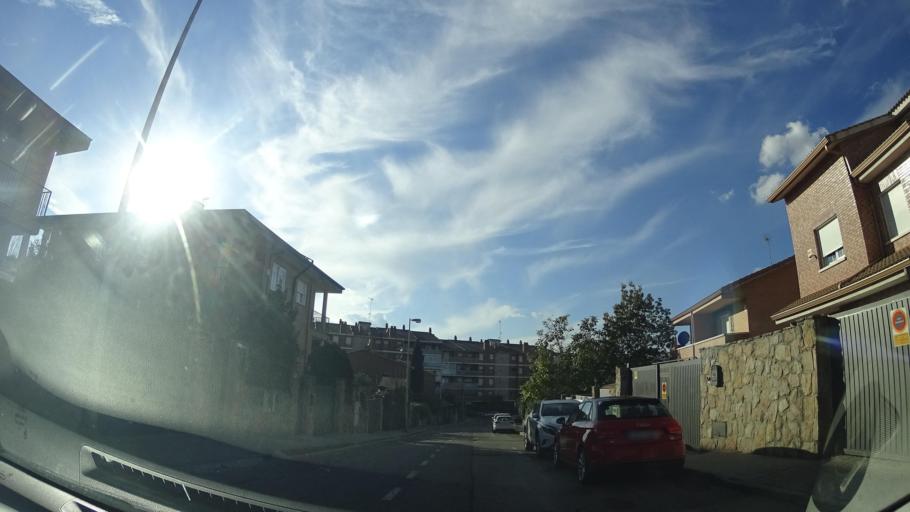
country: ES
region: Madrid
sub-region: Provincia de Madrid
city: Colmenarejo
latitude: 40.5630
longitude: -4.0189
